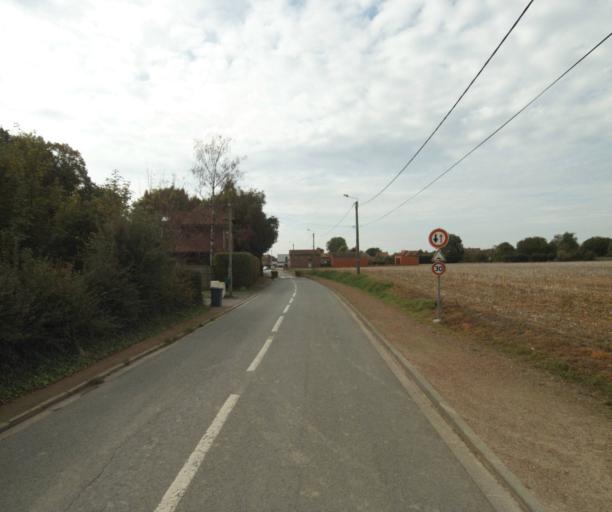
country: FR
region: Nord-Pas-de-Calais
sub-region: Departement du Nord
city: Marquillies
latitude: 50.5554
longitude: 2.8761
